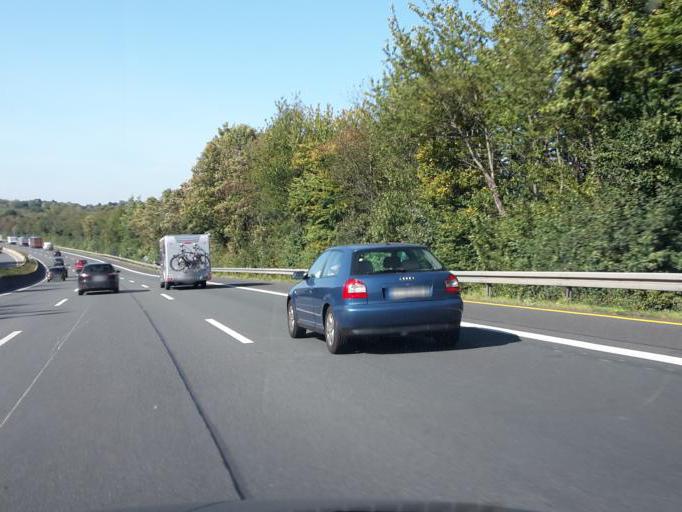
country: DE
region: Rheinland-Pfalz
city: Windhagen
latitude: 50.6647
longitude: 7.3169
